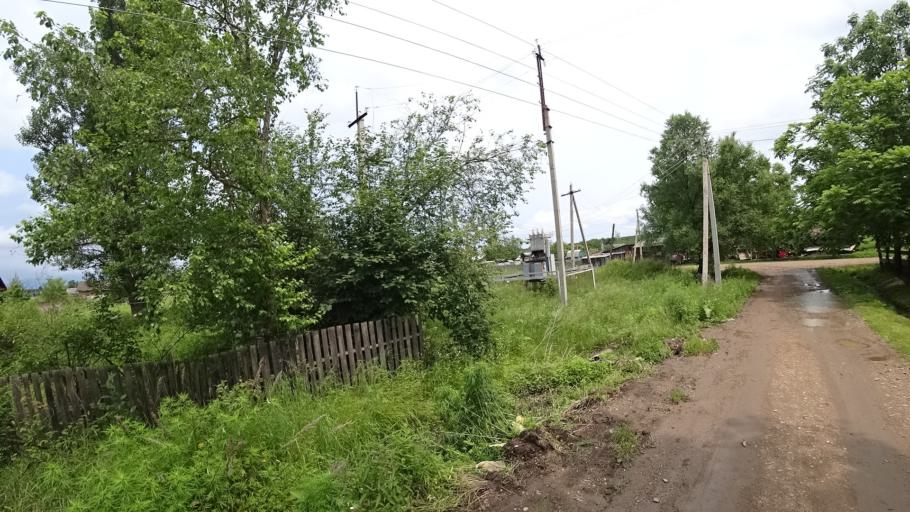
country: RU
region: Primorskiy
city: Novosysoyevka
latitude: 44.2298
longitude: 133.3718
